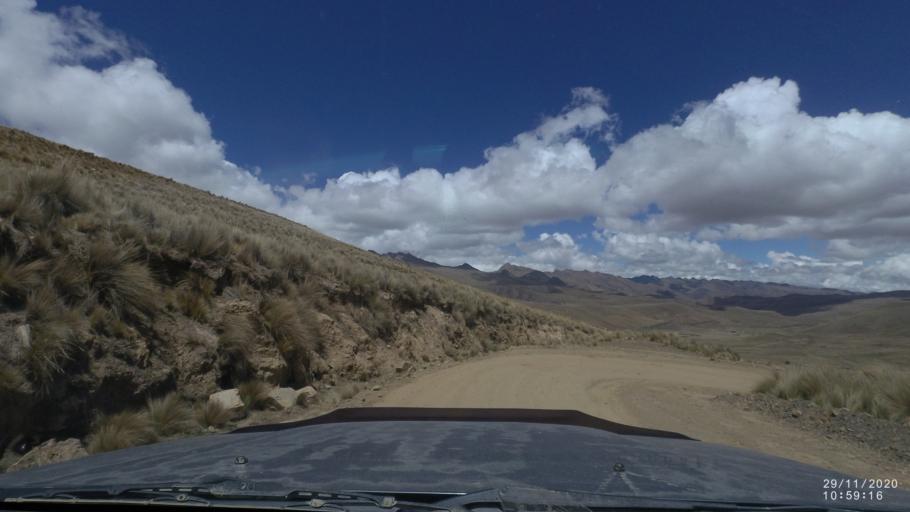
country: BO
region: Cochabamba
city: Cochabamba
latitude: -17.2083
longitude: -66.2277
